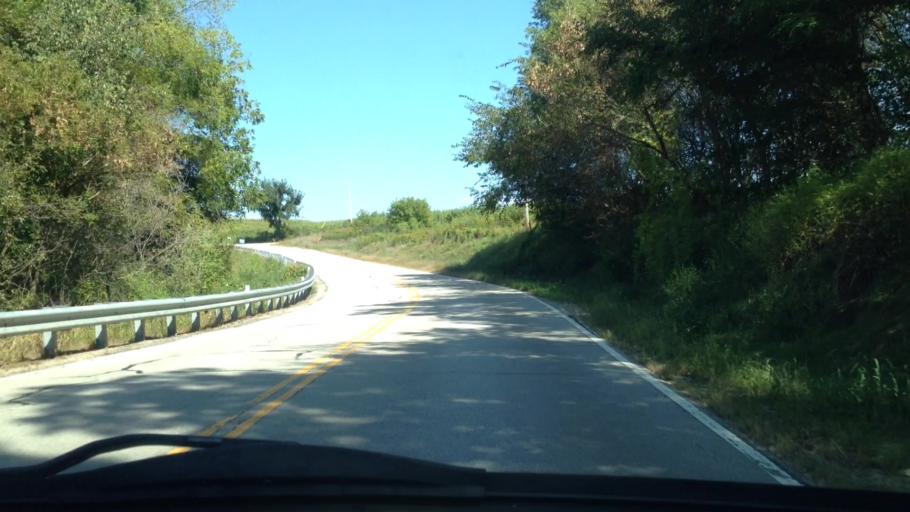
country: US
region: Minnesota
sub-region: Fillmore County
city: Rushford
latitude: 43.6875
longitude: -91.7775
